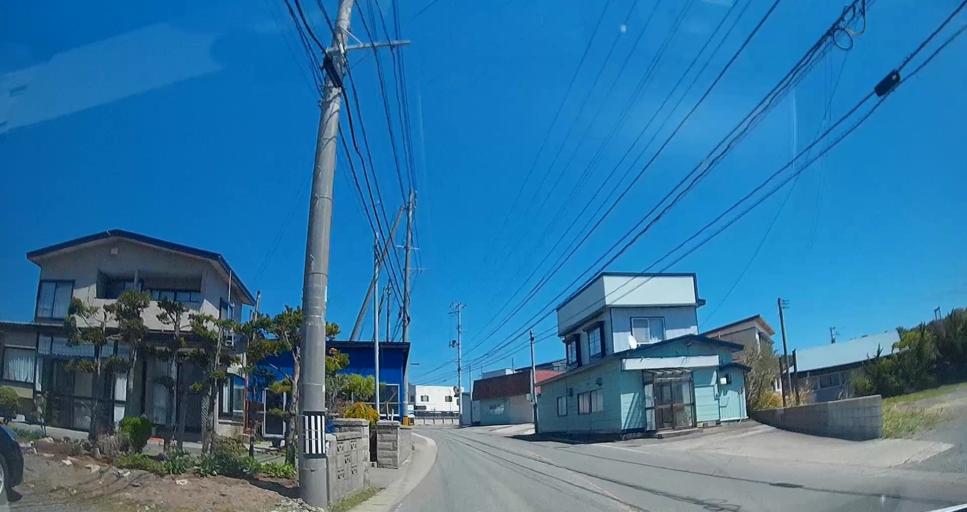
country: JP
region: Aomori
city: Misawa
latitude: 40.9629
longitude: 141.3742
